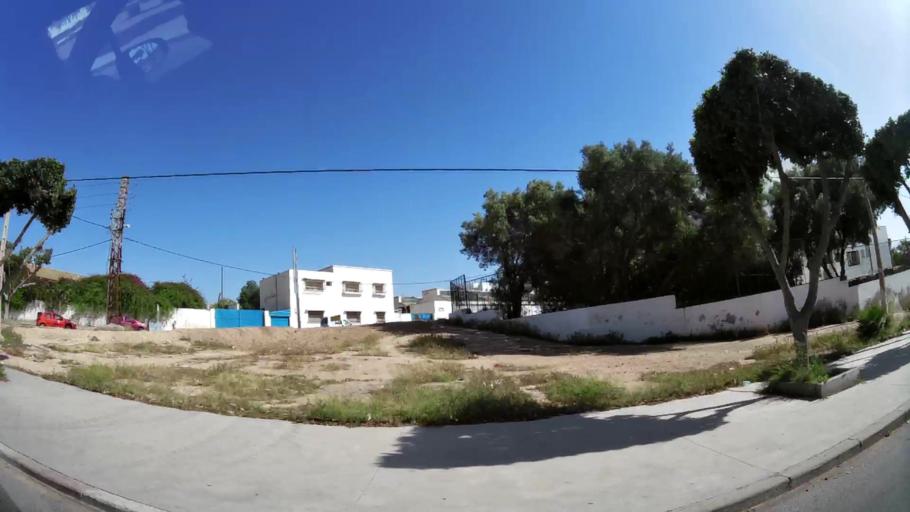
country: MA
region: Souss-Massa-Draa
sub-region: Agadir-Ida-ou-Tnan
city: Agadir
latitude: 30.4208
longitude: -9.5857
